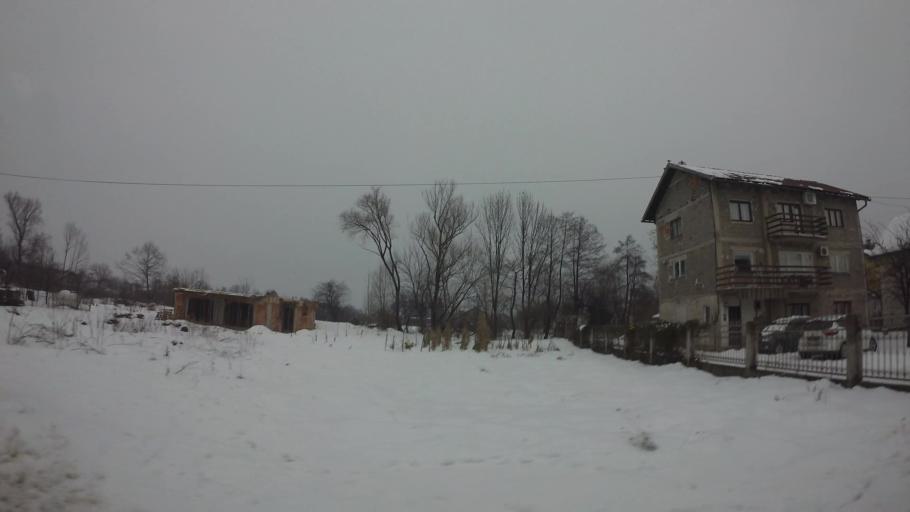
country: BA
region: Federation of Bosnia and Herzegovina
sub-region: Kanton Sarajevo
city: Sarajevo
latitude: 43.8427
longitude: 18.3018
